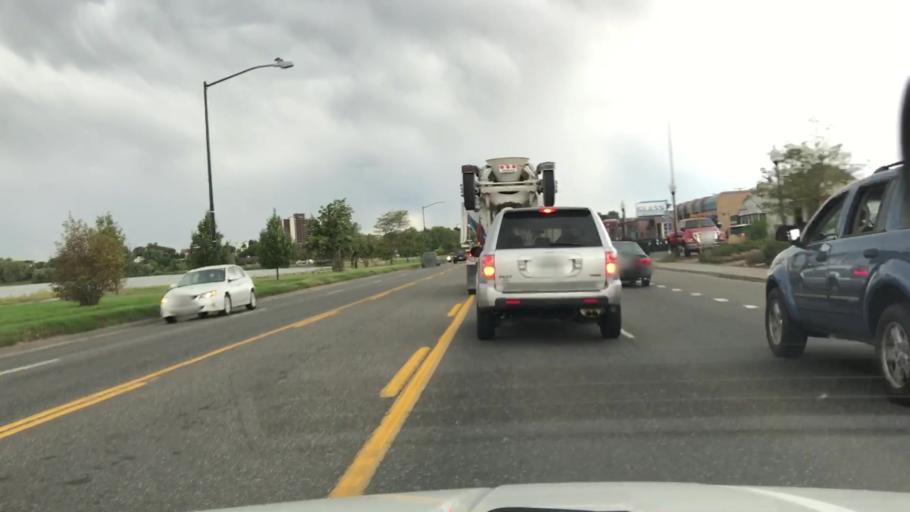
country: US
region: Colorado
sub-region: Jefferson County
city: Edgewater
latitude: 39.7507
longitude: -105.0533
